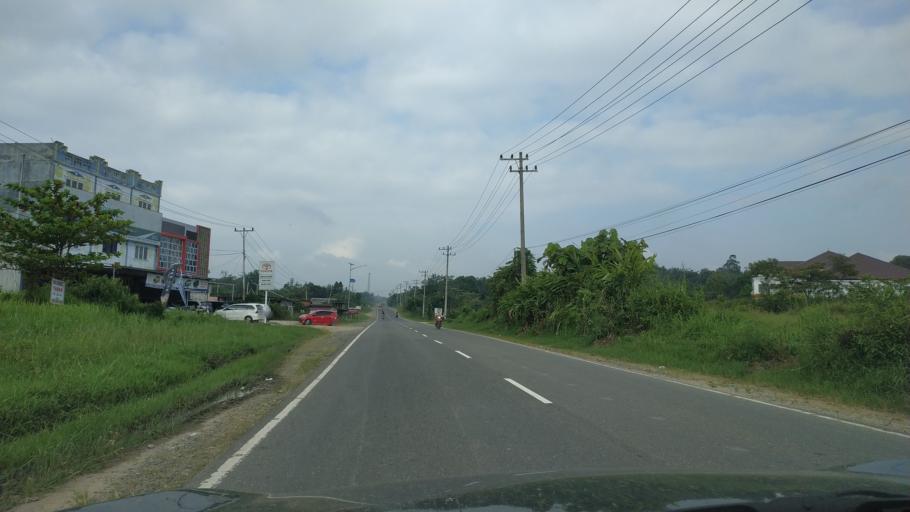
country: ID
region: Riau
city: Rengat
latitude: -0.3944
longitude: 102.4313
